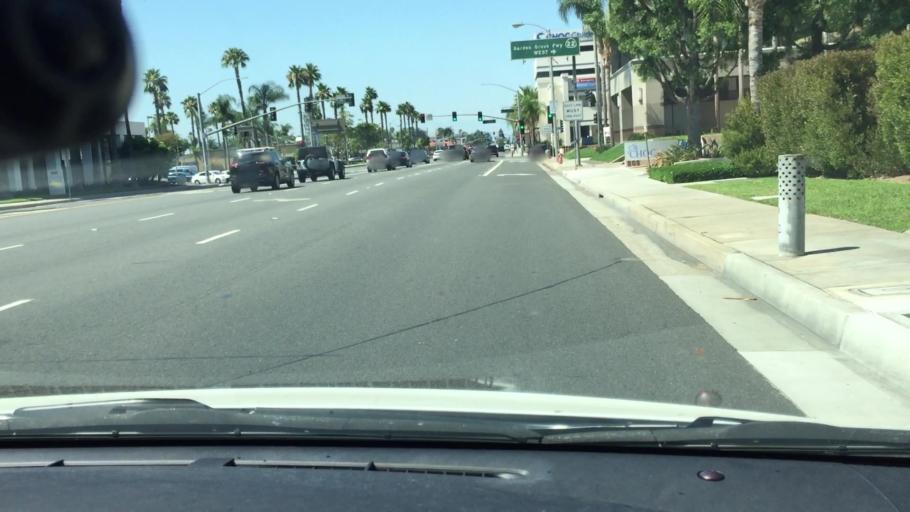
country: US
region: California
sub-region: Orange County
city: Orange
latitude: 33.7794
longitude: -117.8672
